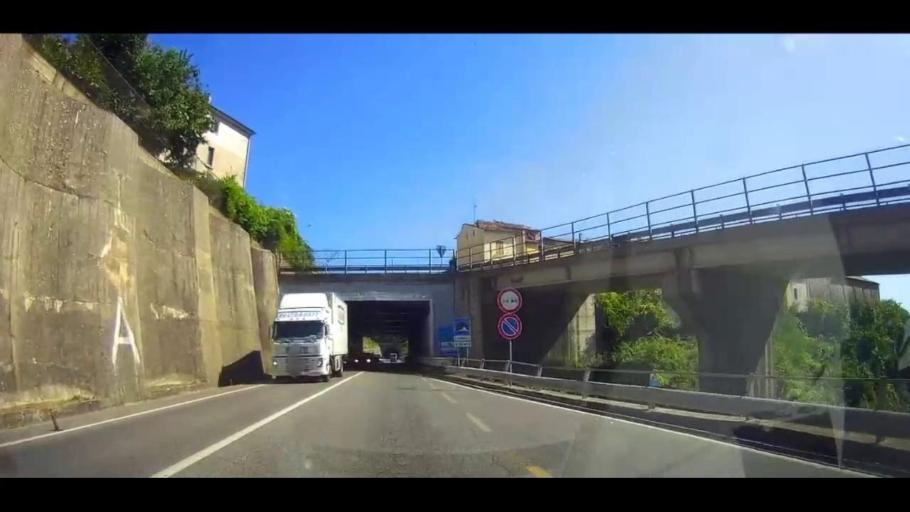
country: IT
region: Calabria
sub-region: Provincia di Cosenza
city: Celico
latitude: 39.3152
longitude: 16.3379
